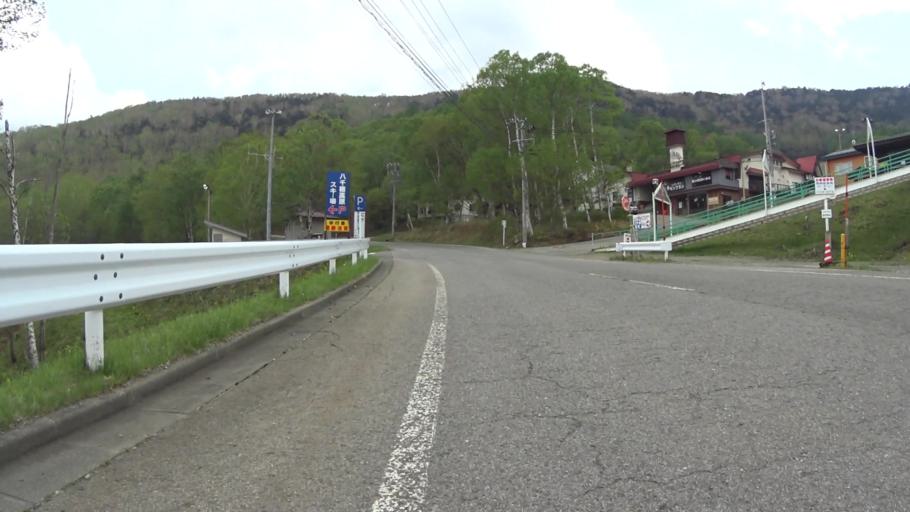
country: JP
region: Nagano
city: Saku
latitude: 36.0702
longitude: 138.3810
